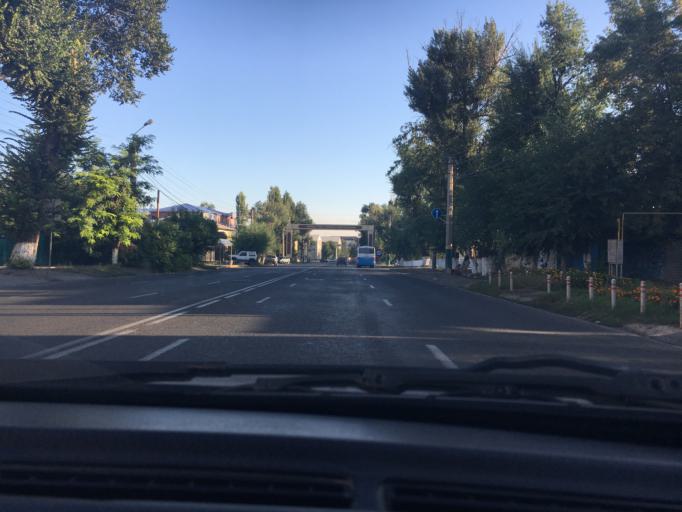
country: KZ
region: Zhambyl
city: Taraz
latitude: 42.8982
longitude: 71.3602
